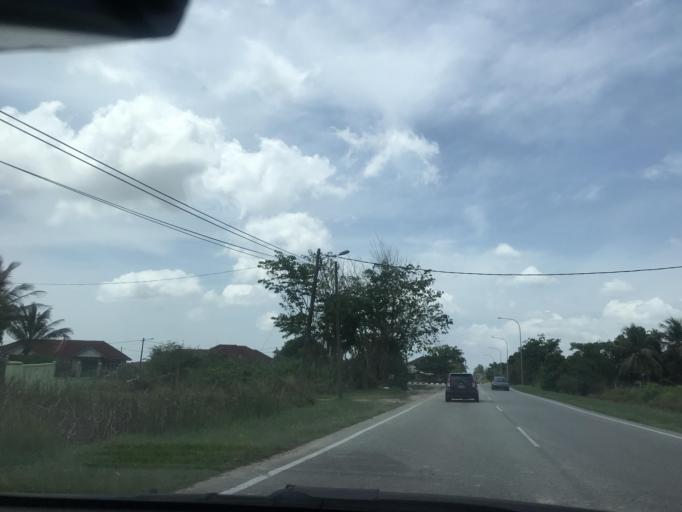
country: MY
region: Kelantan
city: Kota Bharu
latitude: 6.1498
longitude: 102.2123
